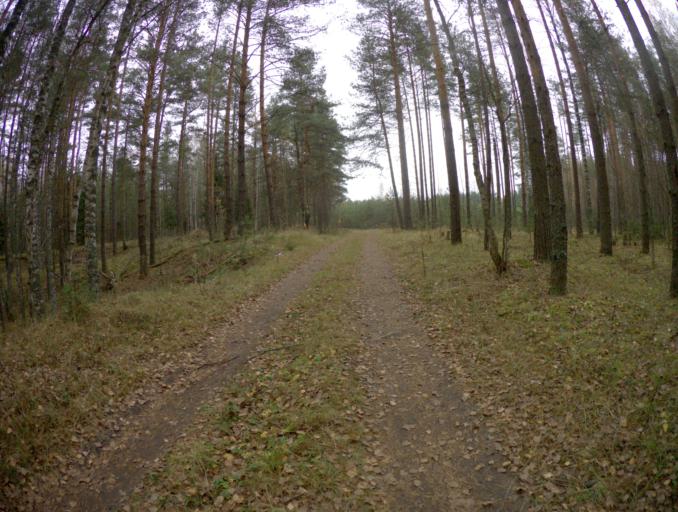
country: RU
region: Vladimir
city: Krasnyy Oktyabr'
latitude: 56.0064
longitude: 38.8354
